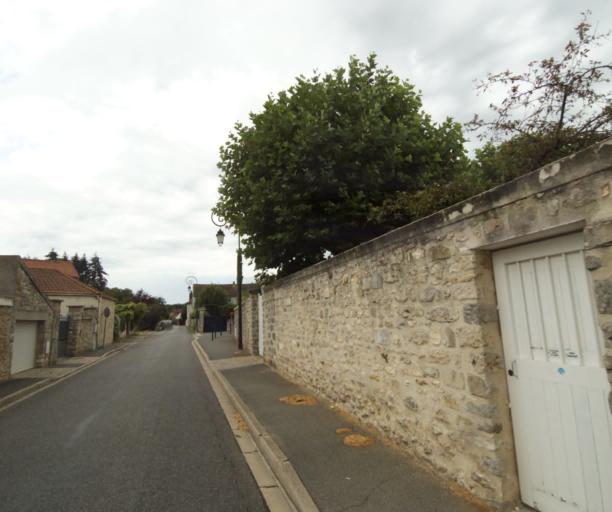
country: FR
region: Ile-de-France
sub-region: Departement de l'Essonne
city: Soisy-sur-Ecole
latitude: 48.4780
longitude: 2.4961
